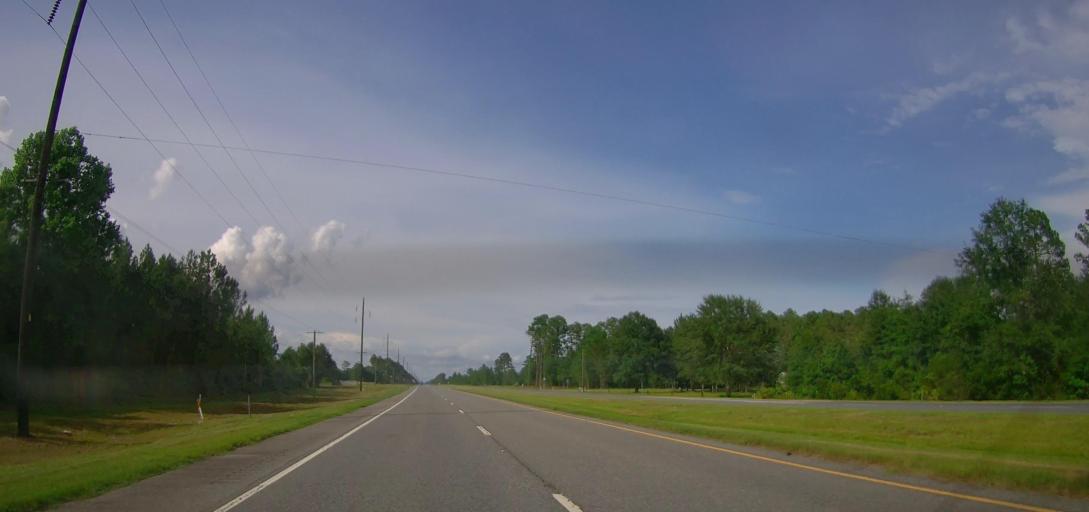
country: US
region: Georgia
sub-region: Wayne County
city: Jesup
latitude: 31.5292
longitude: -81.9850
